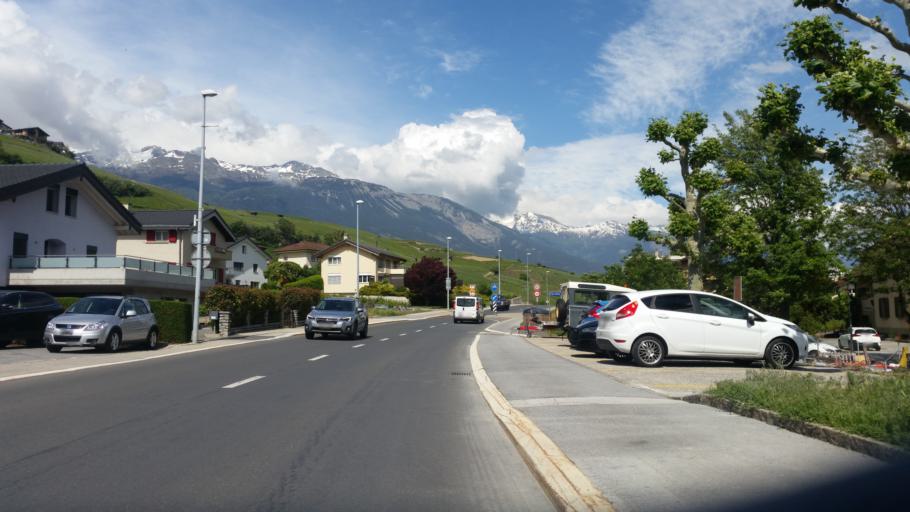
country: CH
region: Valais
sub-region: Sierre District
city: Chalais
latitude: 46.2818
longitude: 7.5069
